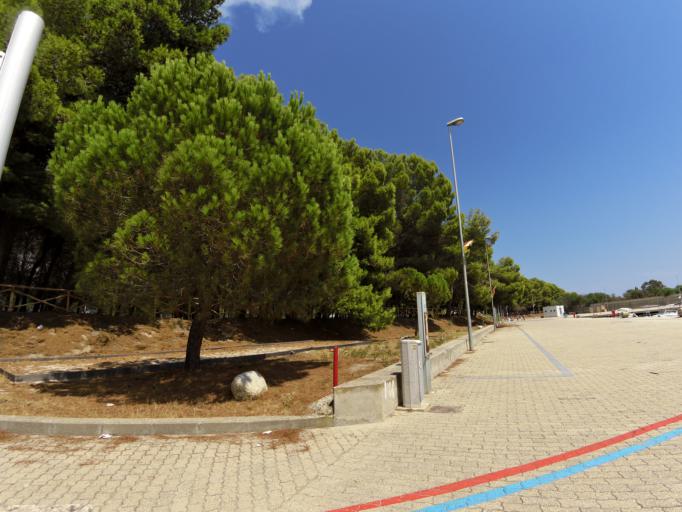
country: IT
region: Calabria
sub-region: Provincia di Reggio Calabria
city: Caulonia Marina
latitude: 38.3293
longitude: 16.4346
